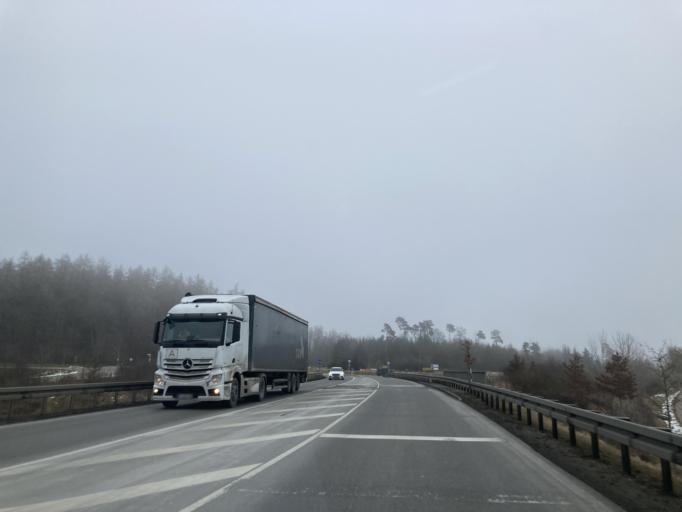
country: DE
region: Baden-Wuerttemberg
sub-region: Freiburg Region
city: Emmingen-Liptingen
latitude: 47.9497
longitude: 8.8913
